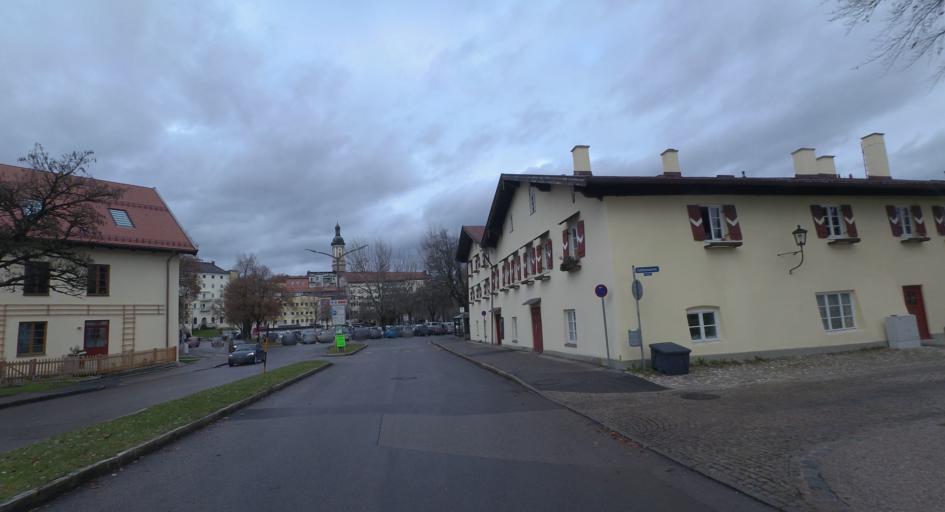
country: DE
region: Bavaria
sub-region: Upper Bavaria
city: Traunstein
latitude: 47.8677
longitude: 12.6458
